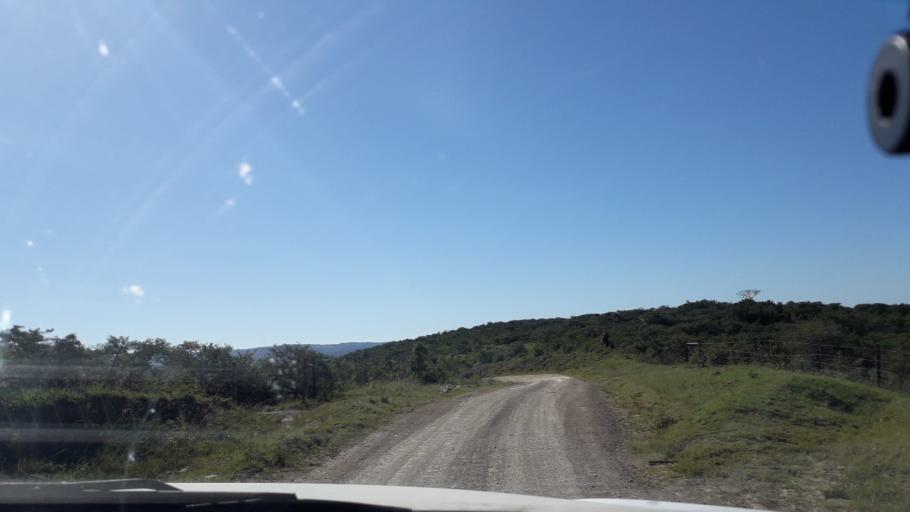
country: ZA
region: Eastern Cape
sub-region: Amathole District Municipality
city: Komga
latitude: -32.7823
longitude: 27.9567
